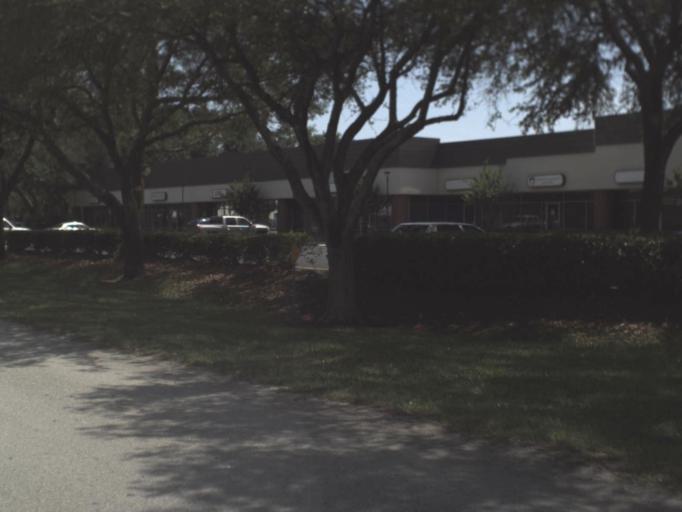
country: US
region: Florida
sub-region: Duval County
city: Jacksonville
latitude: 30.2851
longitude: -81.6319
